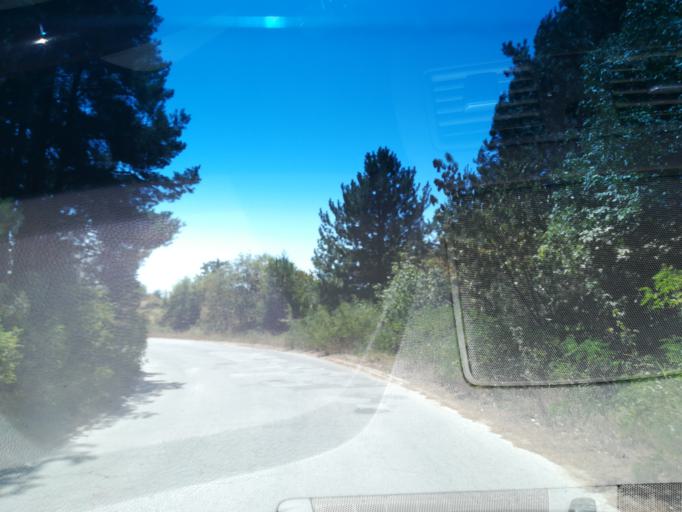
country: BG
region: Pazardzhik
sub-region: Obshtina Strelcha
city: Strelcha
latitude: 42.5392
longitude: 24.3332
